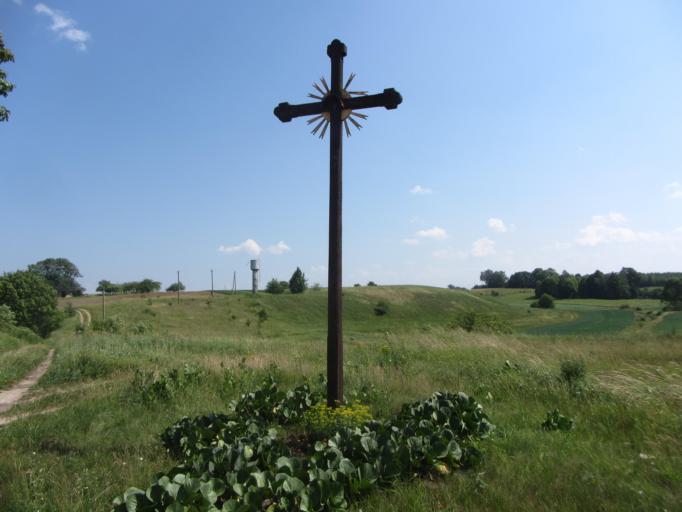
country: LT
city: Lazdijai
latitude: 54.2263
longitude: 23.5797
